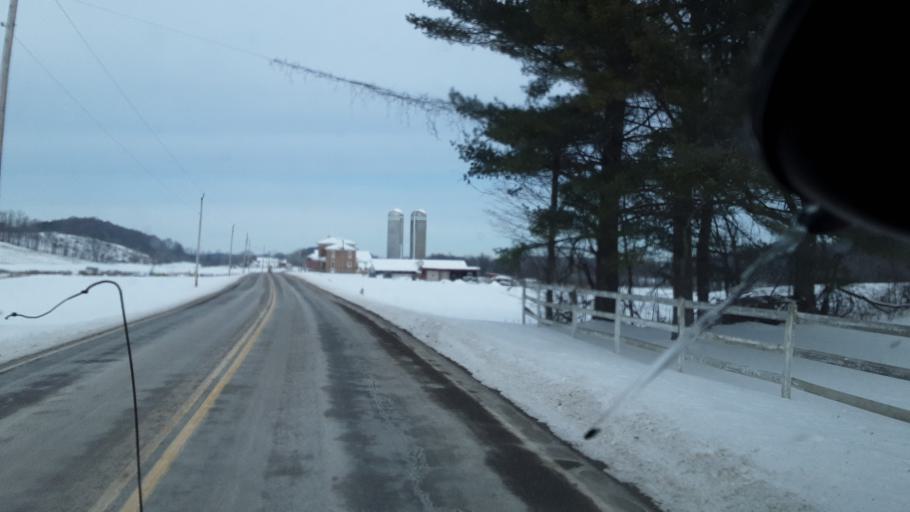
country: US
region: New York
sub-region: Wayne County
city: Newark
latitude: 43.0748
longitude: -77.0567
